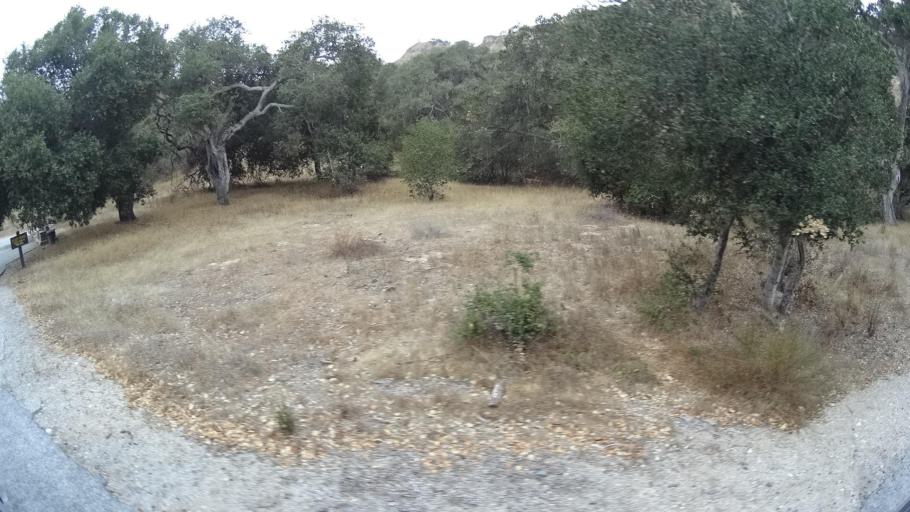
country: US
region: California
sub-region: Monterey County
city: Salinas
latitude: 36.5885
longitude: -121.6894
